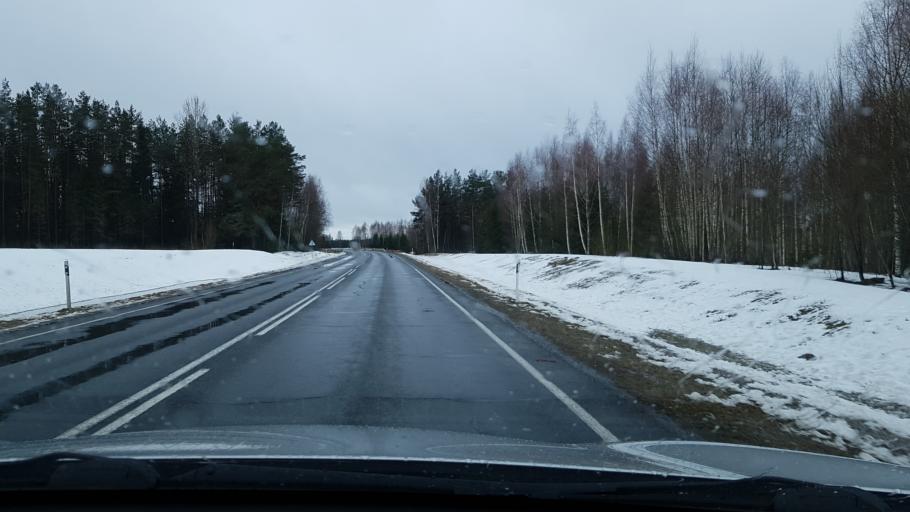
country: LV
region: Apes Novads
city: Ape
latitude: 57.6954
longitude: 26.7318
